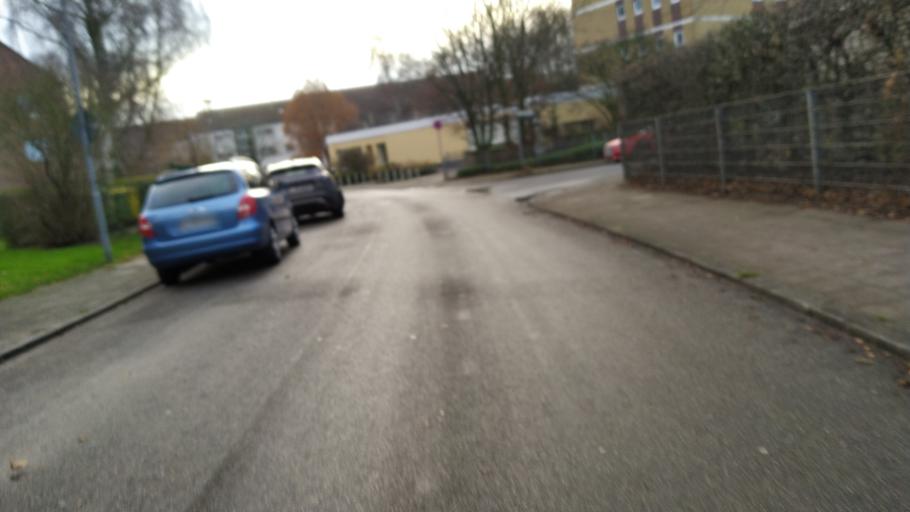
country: DE
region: Schleswig-Holstein
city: Travemuende
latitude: 53.9668
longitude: 10.8661
